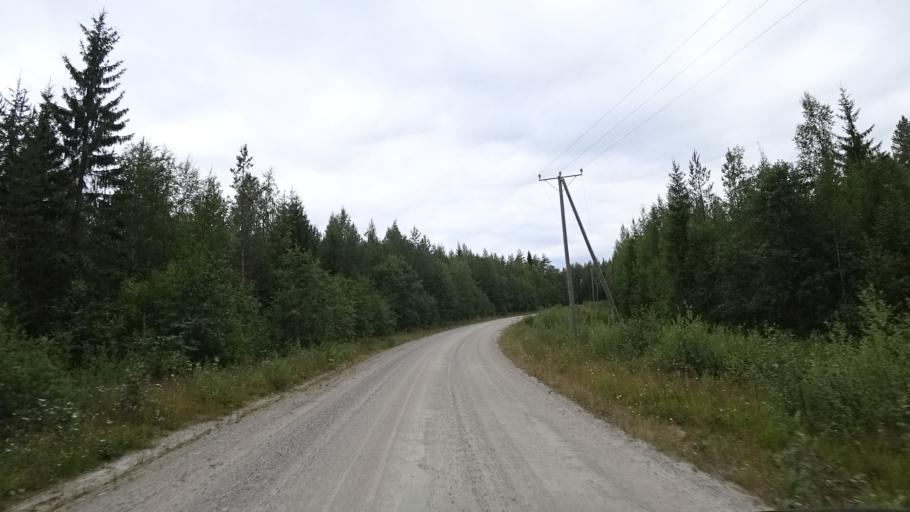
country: FI
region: North Karelia
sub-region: Joensuu
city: Eno
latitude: 63.1741
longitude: 30.5551
